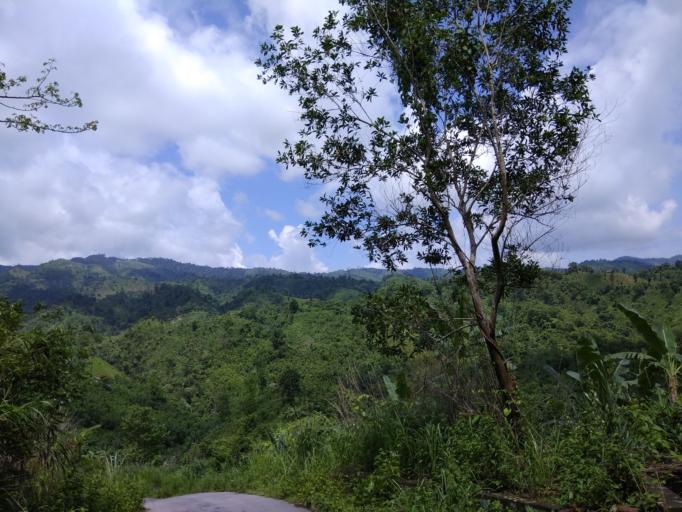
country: BD
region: Chittagong
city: Satkania
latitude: 21.7197
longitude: 92.3858
